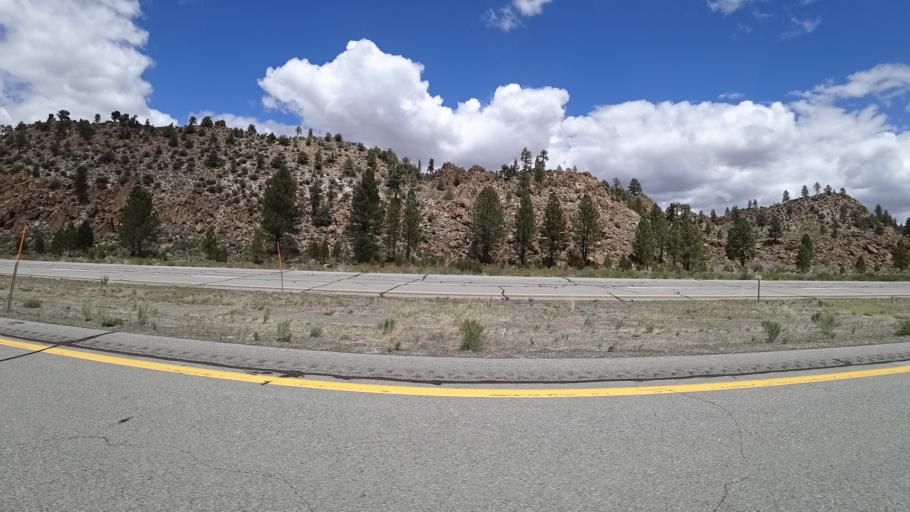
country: US
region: California
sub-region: Mono County
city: Mammoth Lakes
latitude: 37.5708
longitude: -118.6959
